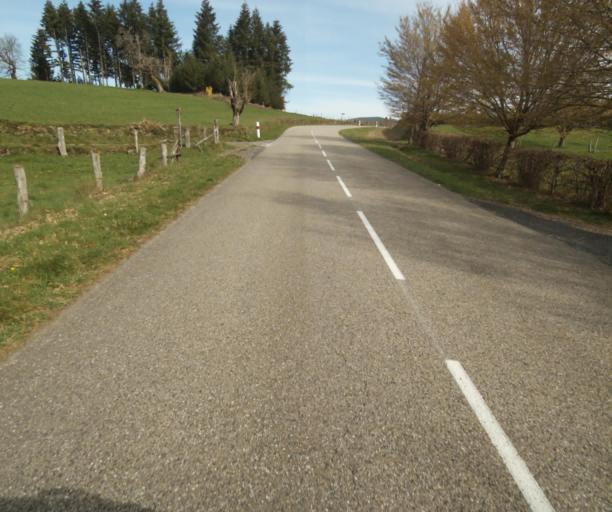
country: FR
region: Limousin
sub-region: Departement de la Correze
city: Correze
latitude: 45.4110
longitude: 1.8264
